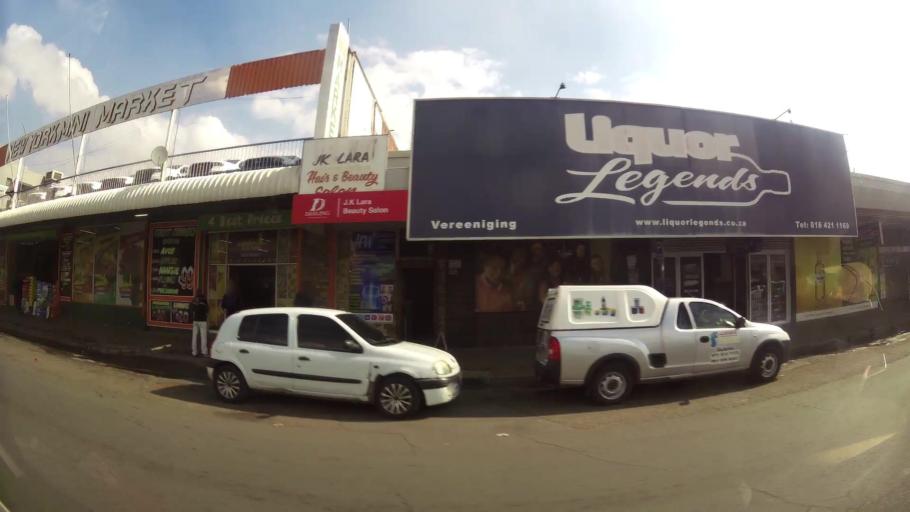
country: ZA
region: Gauteng
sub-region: Sedibeng District Municipality
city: Vereeniging
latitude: -26.6702
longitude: 27.9325
